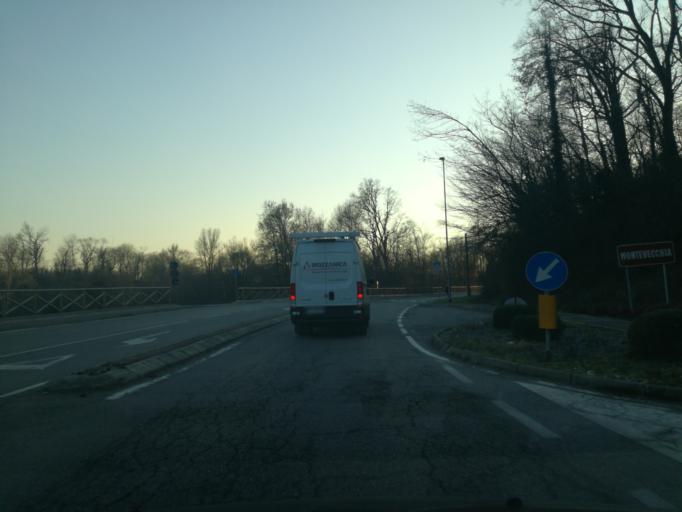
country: IT
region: Lombardy
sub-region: Provincia di Lecco
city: Quattro Strade
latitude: 45.6958
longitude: 9.3850
